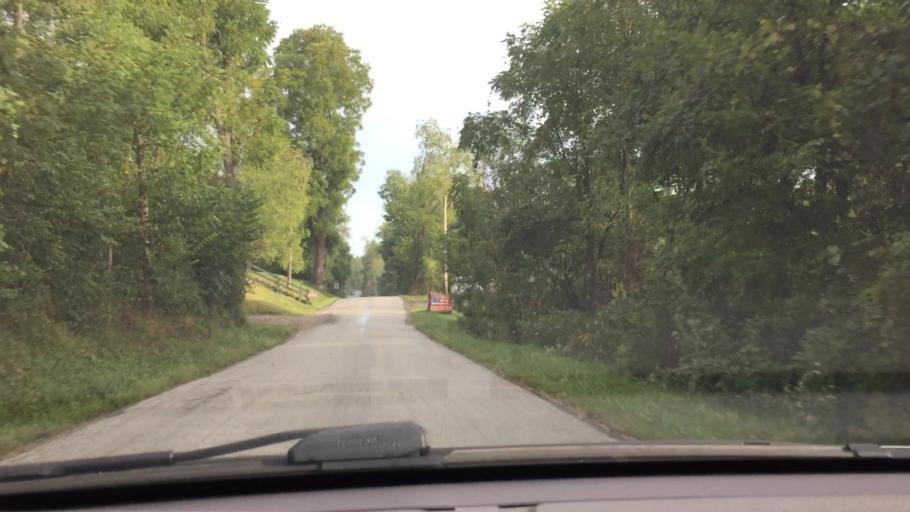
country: US
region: Pennsylvania
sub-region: Washington County
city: McGovern
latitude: 40.1952
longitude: -80.1710
